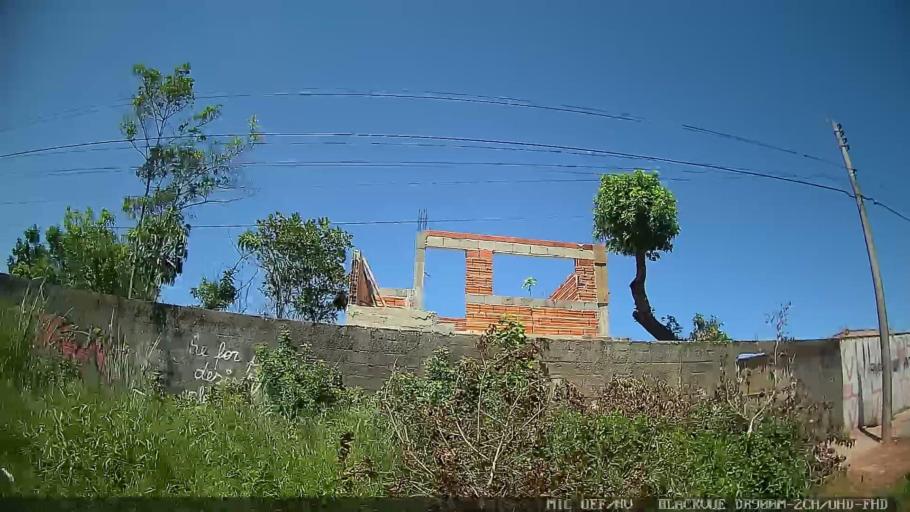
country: BR
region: Sao Paulo
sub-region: Peruibe
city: Peruibe
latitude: -24.3004
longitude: -46.9891
